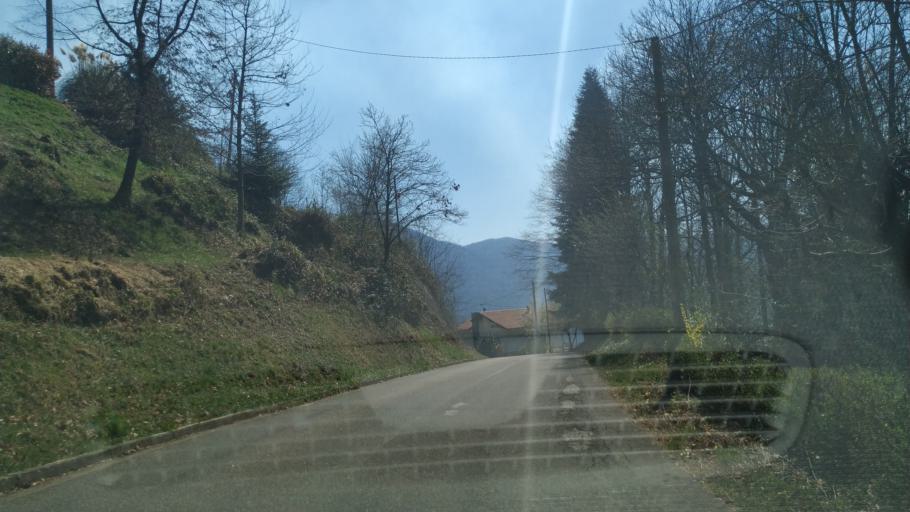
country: IT
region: Piedmont
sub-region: Provincia di Biella
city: Pray
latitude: 45.6800
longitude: 8.2065
